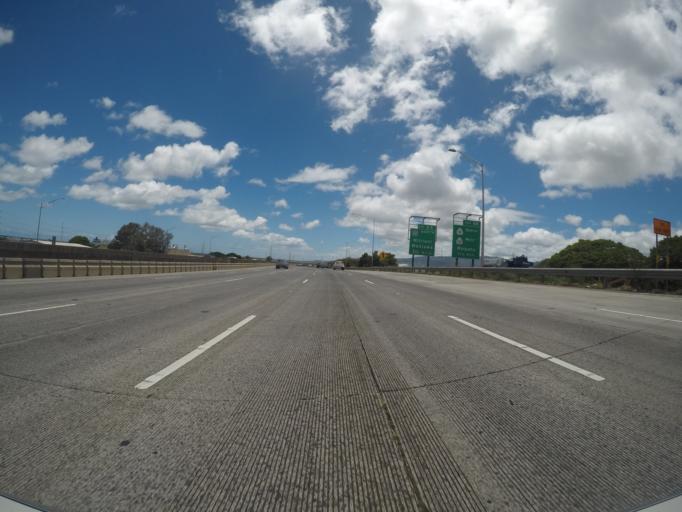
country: US
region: Hawaii
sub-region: Honolulu County
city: Pearl City, Manana
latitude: 21.3931
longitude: -157.9578
